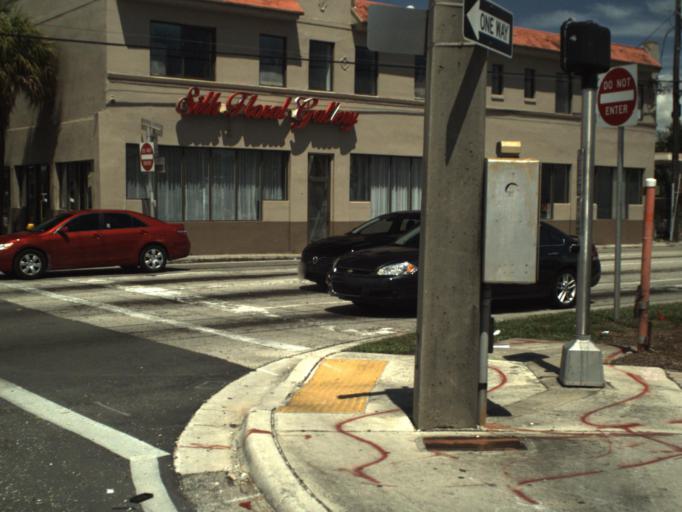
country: US
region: Florida
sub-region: Broward County
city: Hallandale Beach
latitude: 25.9856
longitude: -80.1483
